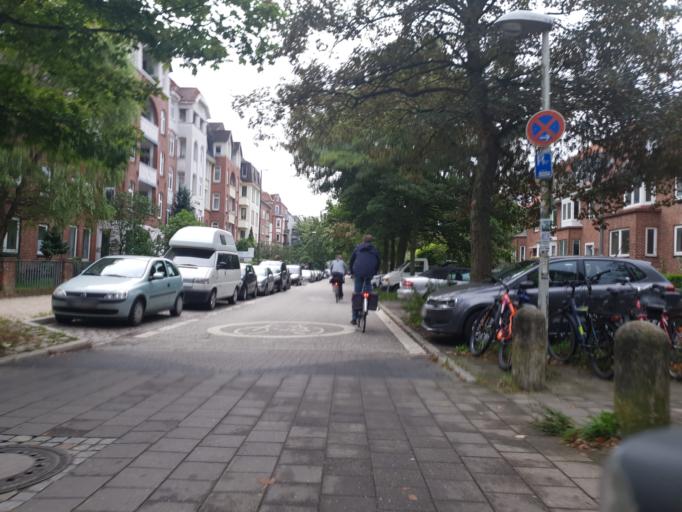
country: DE
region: Schleswig-Holstein
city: Kiel
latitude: 54.3372
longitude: 10.1273
